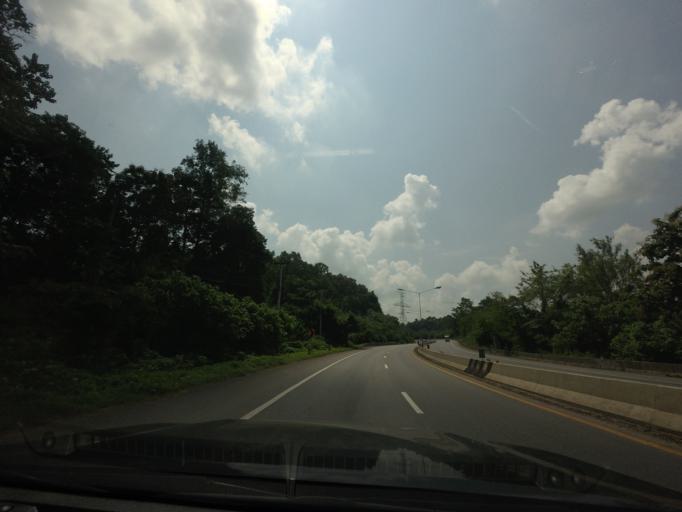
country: TH
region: Uttaradit
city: Lap Lae
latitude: 17.7849
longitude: 100.1185
